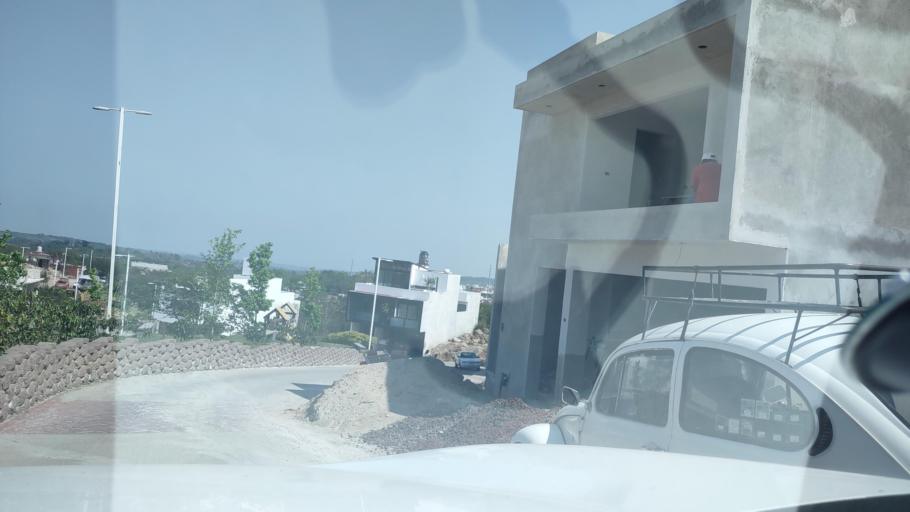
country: MX
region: Veracruz
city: El Castillo
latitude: 19.5285
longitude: -96.8717
